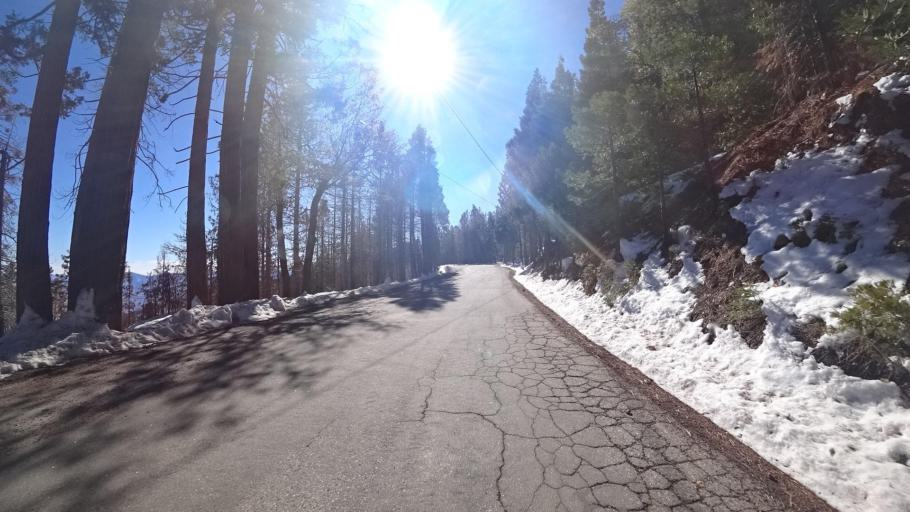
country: US
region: California
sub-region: Kern County
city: Alta Sierra
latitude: 35.7226
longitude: -118.5551
